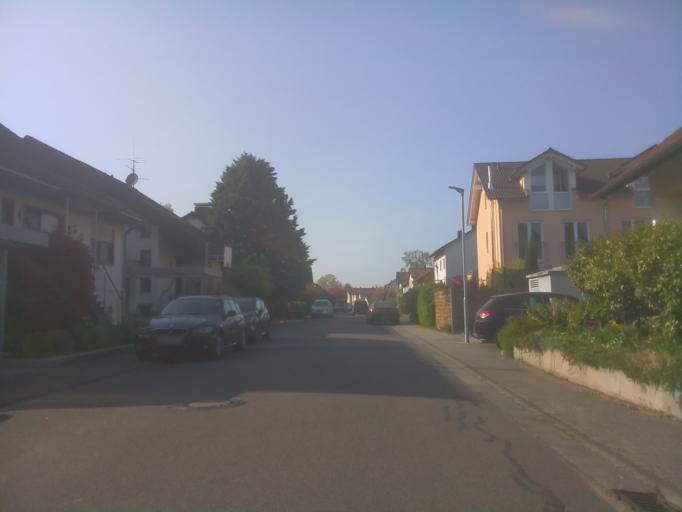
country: DE
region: Baden-Wuerttemberg
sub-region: Karlsruhe Region
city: Weinheim
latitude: 49.5302
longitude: 8.6480
